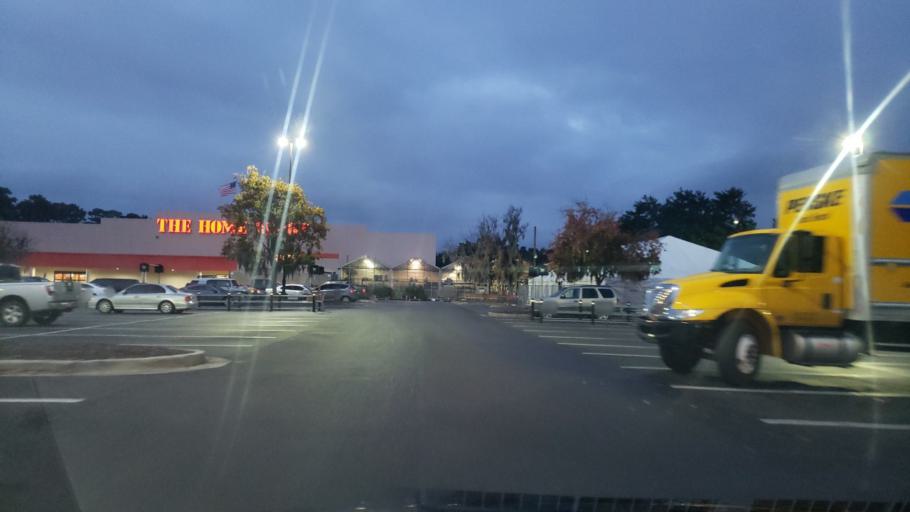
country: US
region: Georgia
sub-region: Chatham County
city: Montgomery
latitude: 31.9818
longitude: -81.1442
